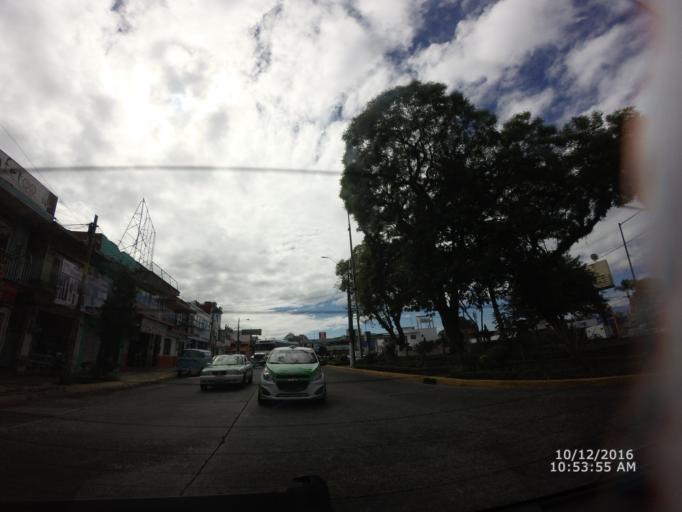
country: MX
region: Veracruz
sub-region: Xalapa
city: Xalapa de Enriquez
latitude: 19.5409
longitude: -96.9260
